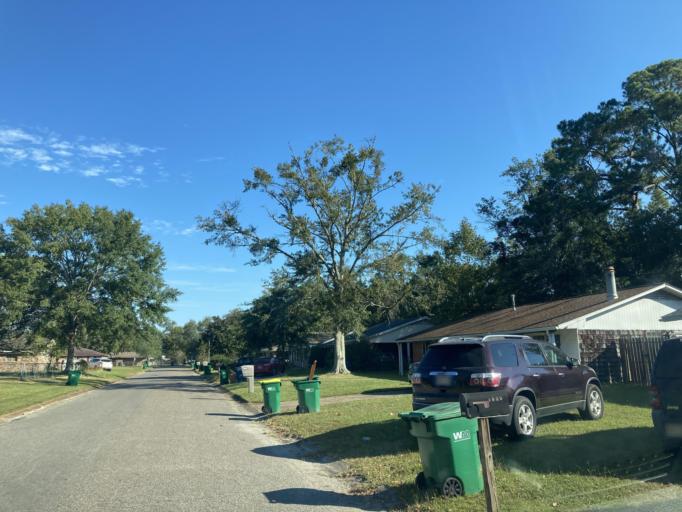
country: US
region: Mississippi
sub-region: Jackson County
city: Saint Martin
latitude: 30.4425
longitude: -88.8797
